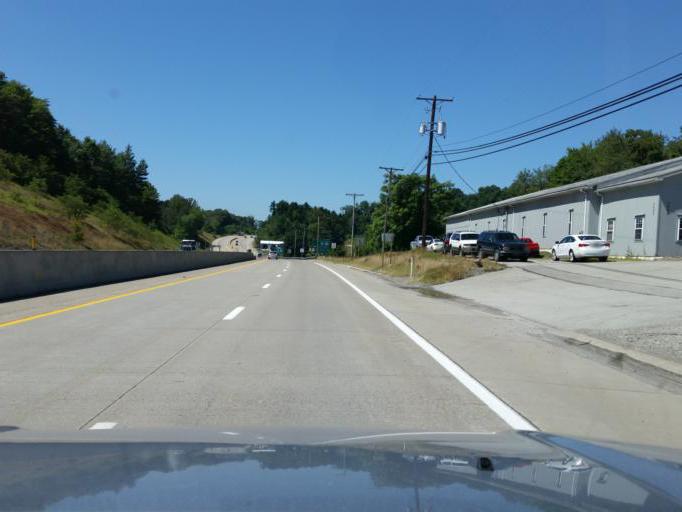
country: US
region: Pennsylvania
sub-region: Indiana County
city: Blairsville
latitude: 40.4248
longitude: -79.3176
